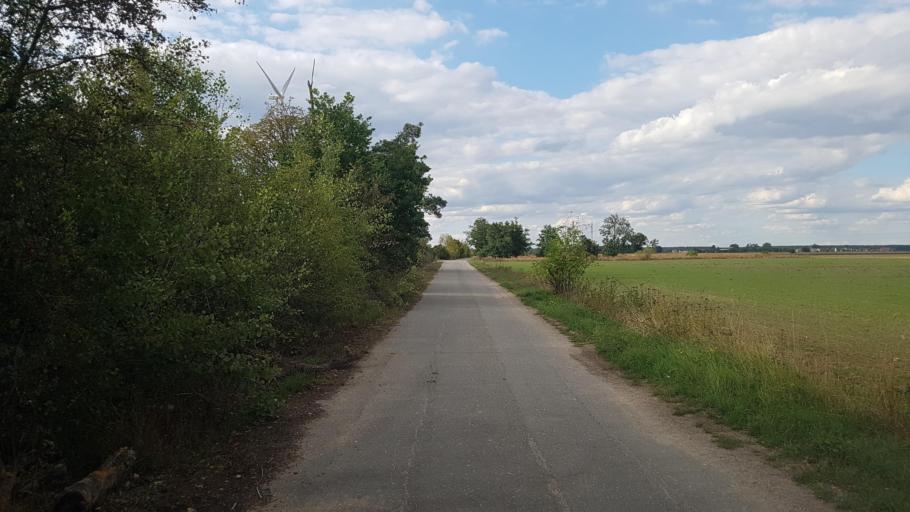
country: DE
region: Saxony
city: Arzberg
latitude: 51.5646
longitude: 13.1710
